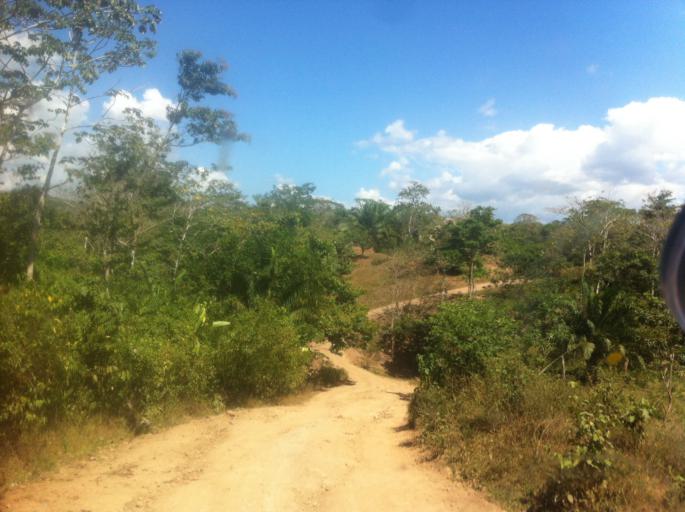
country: CR
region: Alajuela
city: Los Chiles
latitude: 11.2497
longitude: -84.4460
